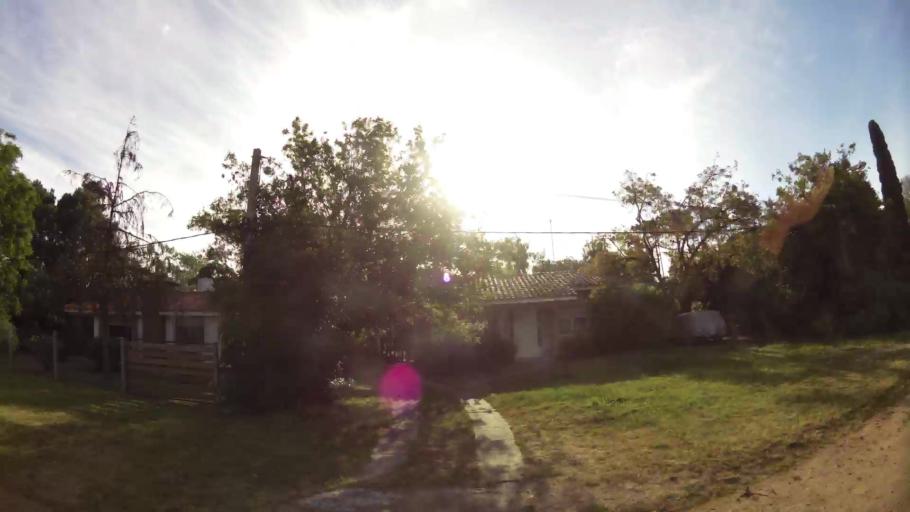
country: UY
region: Canelones
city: Empalme Olmos
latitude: -34.7858
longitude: -55.8551
